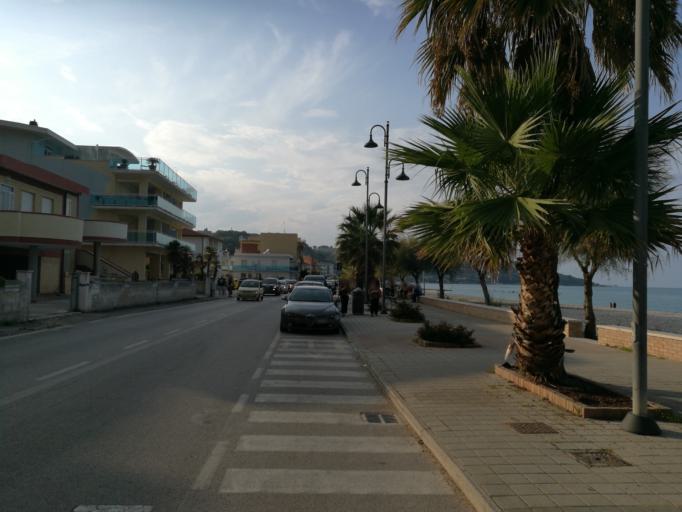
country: IT
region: Abruzzo
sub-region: Provincia di Chieti
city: Fossacesia
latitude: 42.2491
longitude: 14.5125
